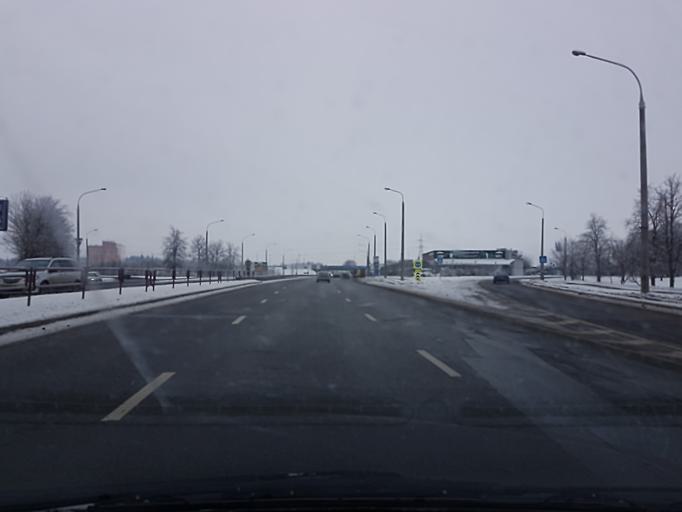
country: BY
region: Minsk
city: Shchomyslitsa
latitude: 53.8460
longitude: 27.4723
